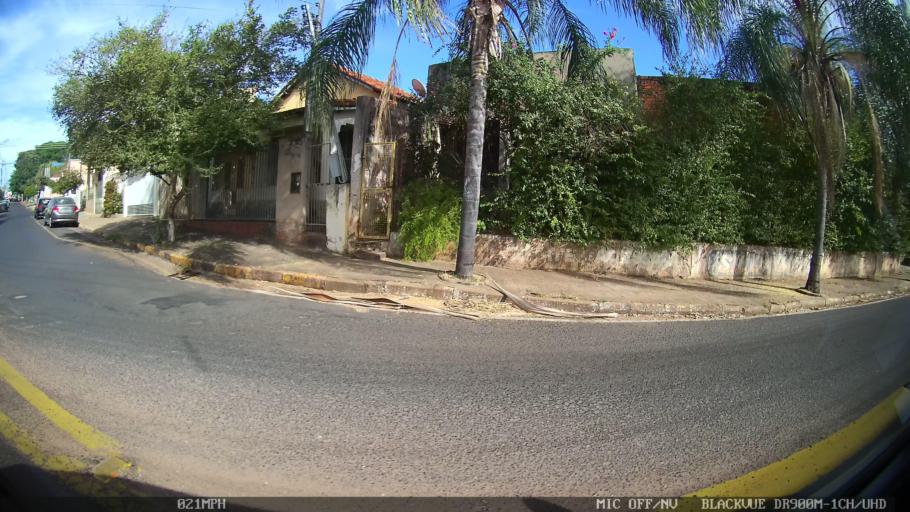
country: BR
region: Sao Paulo
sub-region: Catanduva
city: Catanduva
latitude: -21.1305
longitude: -48.9806
